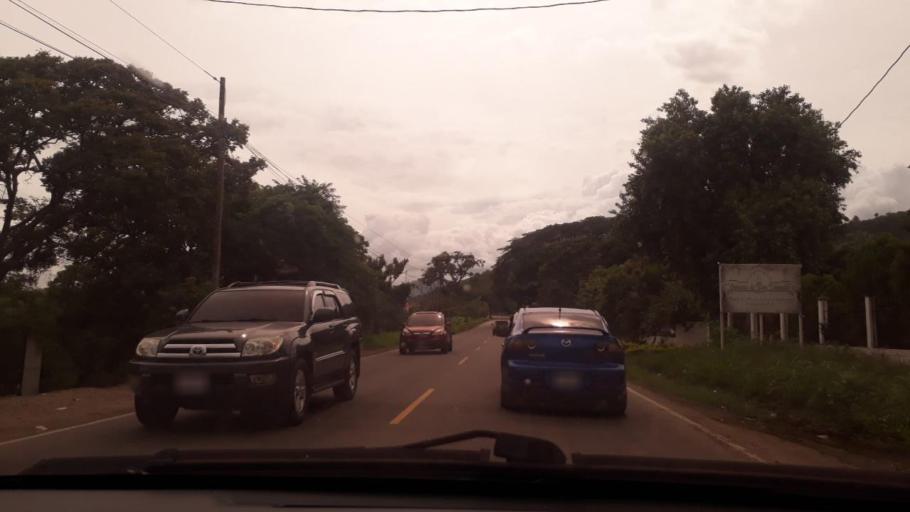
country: GT
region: Jutiapa
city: El Progreso
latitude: 14.3512
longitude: -89.8131
